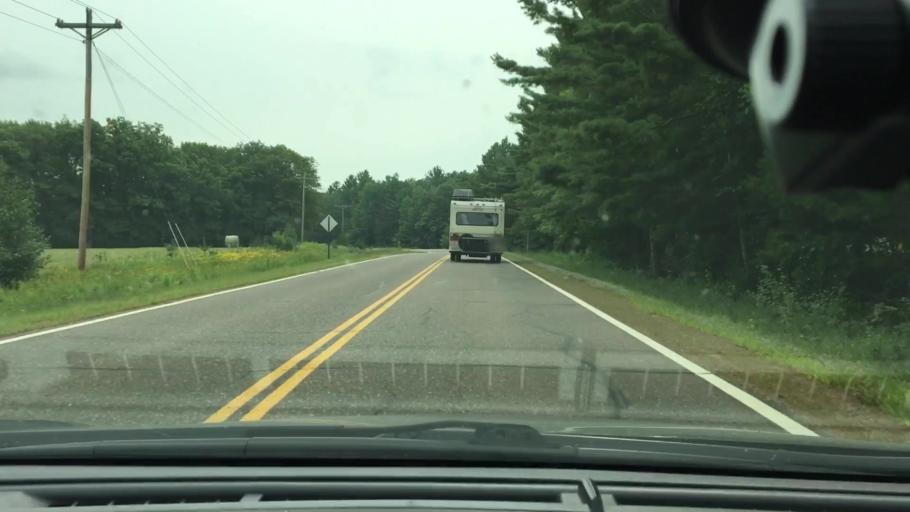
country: US
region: Minnesota
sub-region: Aitkin County
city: Aitkin
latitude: 46.4029
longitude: -93.8032
